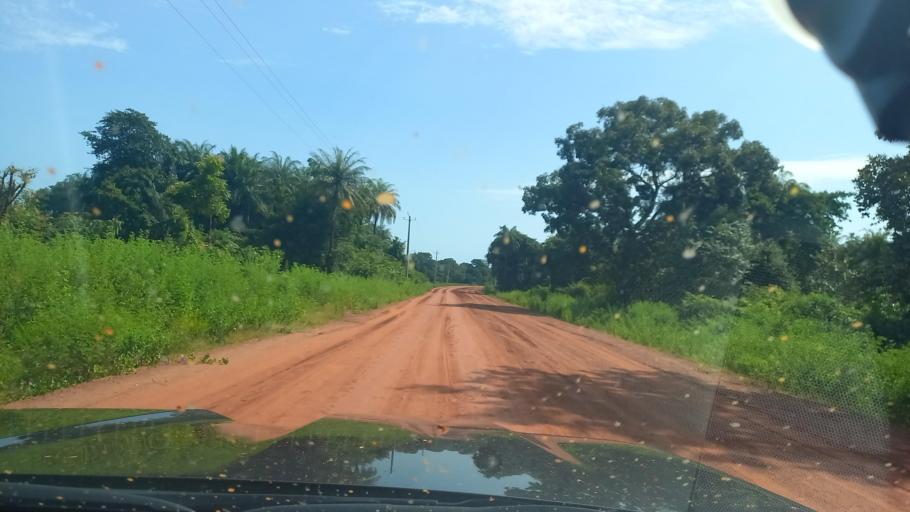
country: SN
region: Ziguinchor
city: Adeane
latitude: 12.6657
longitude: -16.1039
